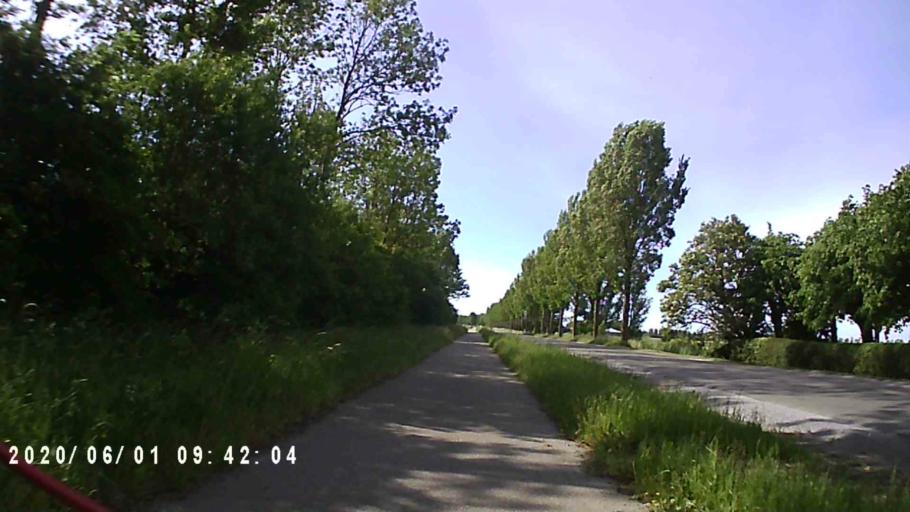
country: NL
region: Friesland
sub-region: Menameradiel
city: Berltsum
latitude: 53.2460
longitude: 5.6826
